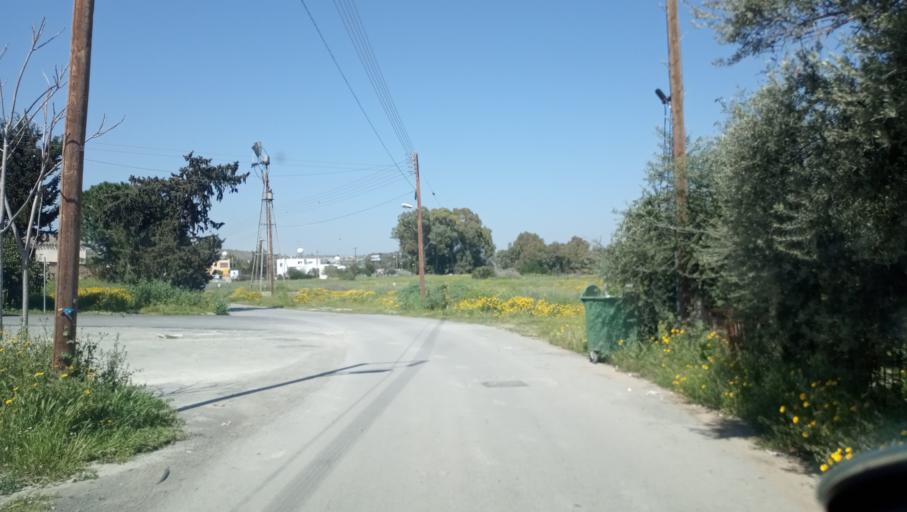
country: CY
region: Lefkosia
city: Alampra
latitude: 35.0145
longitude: 33.3887
